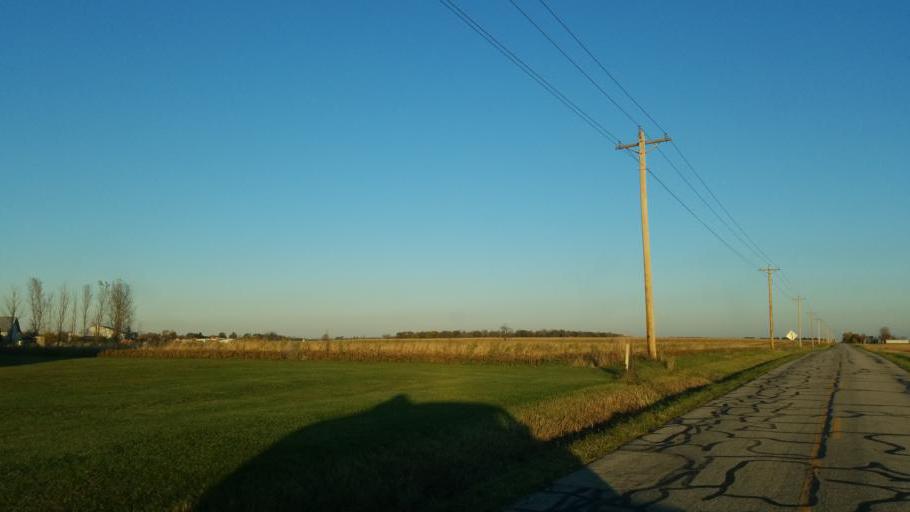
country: US
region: Ohio
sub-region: Sandusky County
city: Mount Carmel
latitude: 41.2121
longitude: -82.9279
